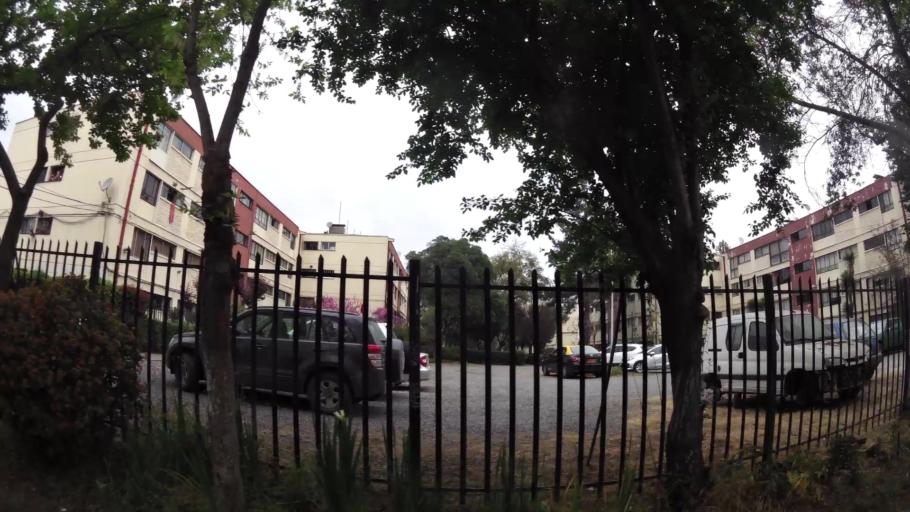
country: CL
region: Santiago Metropolitan
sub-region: Provincia de Santiago
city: Villa Presidente Frei, Nunoa, Santiago, Chile
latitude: -33.4722
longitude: -70.5836
